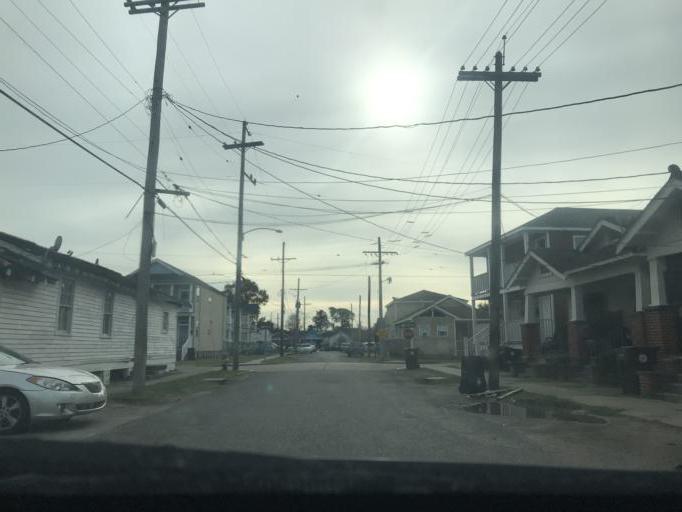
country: US
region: Louisiana
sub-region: Orleans Parish
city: New Orleans
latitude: 29.9573
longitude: -90.1106
